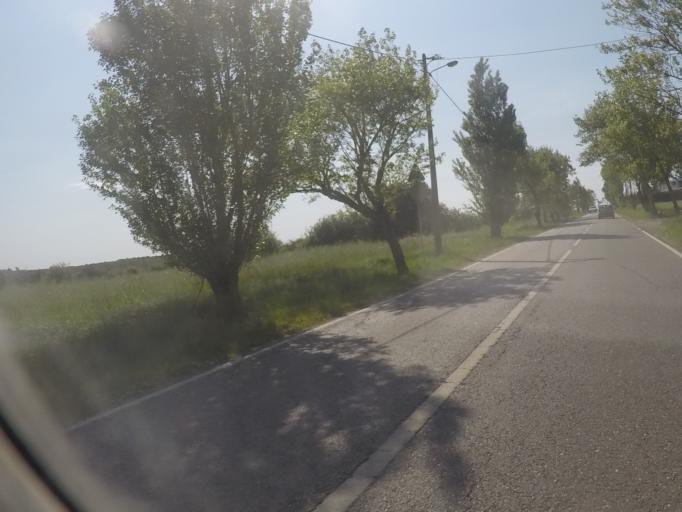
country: PT
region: Setubal
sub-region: Sesimbra
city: Sesimbra
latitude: 38.4449
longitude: -9.1498
